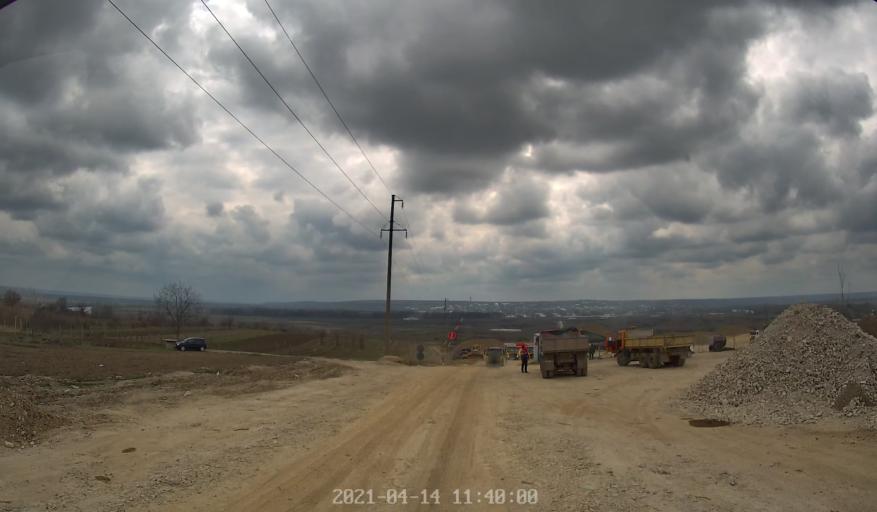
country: MD
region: Criuleni
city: Criuleni
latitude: 47.1661
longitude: 29.1857
